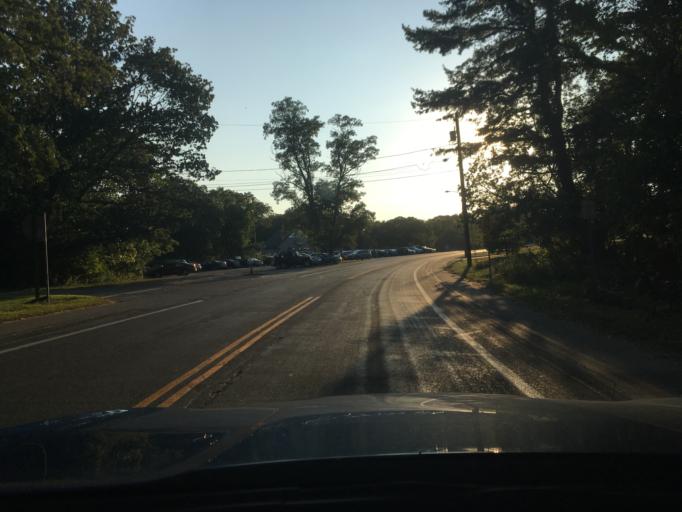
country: US
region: Rhode Island
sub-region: Kent County
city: East Greenwich
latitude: 41.6452
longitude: -71.4491
